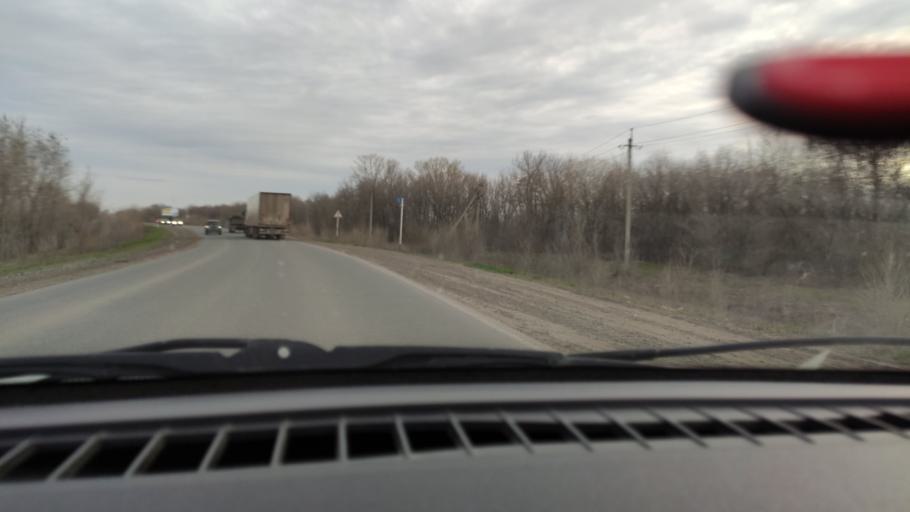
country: RU
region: Orenburg
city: Tatarskaya Kargala
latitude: 51.8953
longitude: 55.1604
